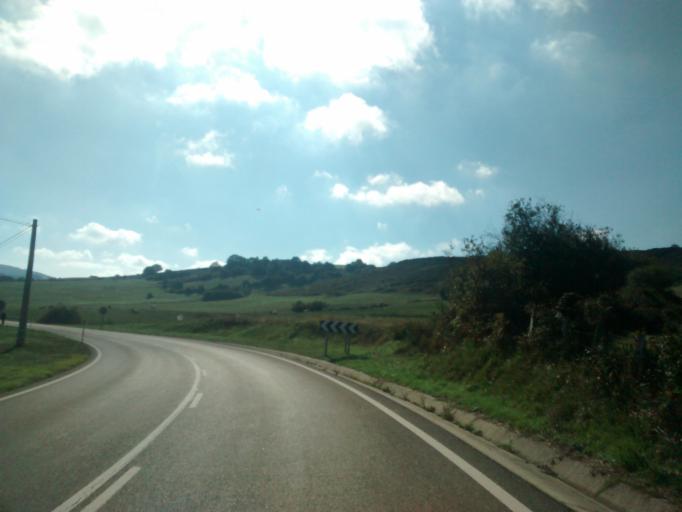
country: ES
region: Cantabria
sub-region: Provincia de Cantabria
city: Reinosa
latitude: 42.9699
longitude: -4.0707
